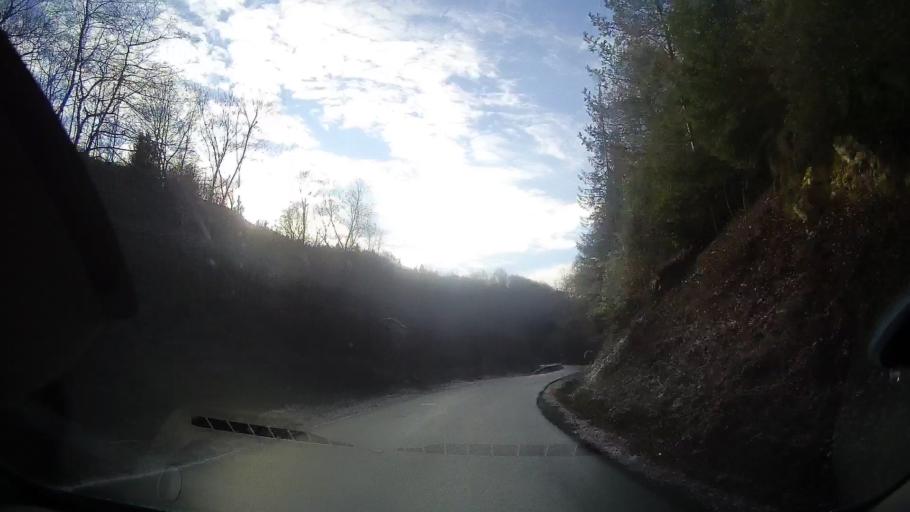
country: RO
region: Alba
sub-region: Comuna Sohodol
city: Sohodol
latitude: 46.3481
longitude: 23.0202
